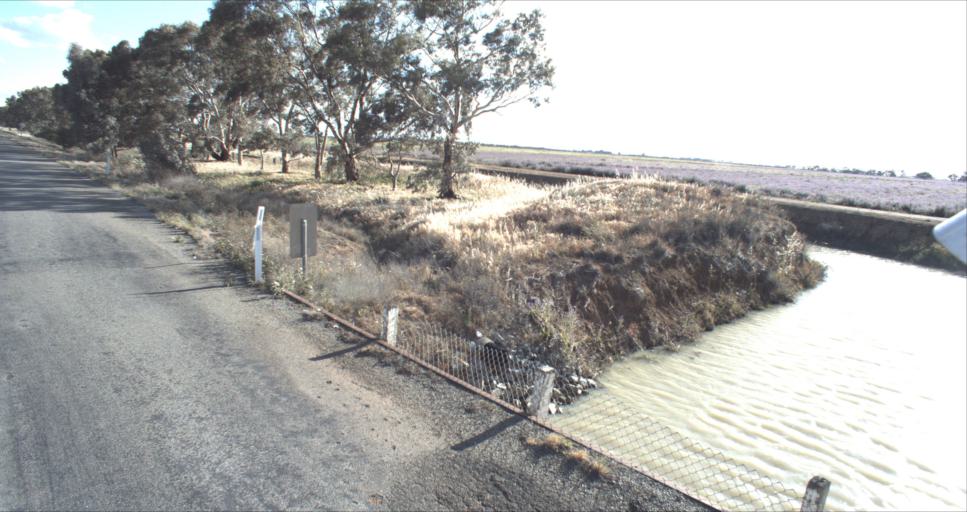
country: AU
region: New South Wales
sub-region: Leeton
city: Leeton
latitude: -34.5411
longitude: 146.2799
